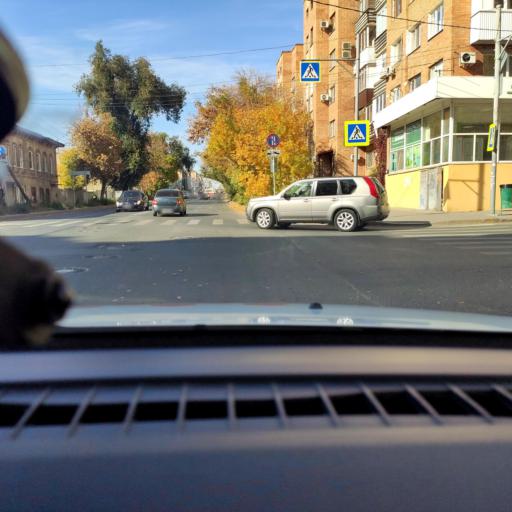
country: RU
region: Samara
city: Samara
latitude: 53.1828
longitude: 50.0987
